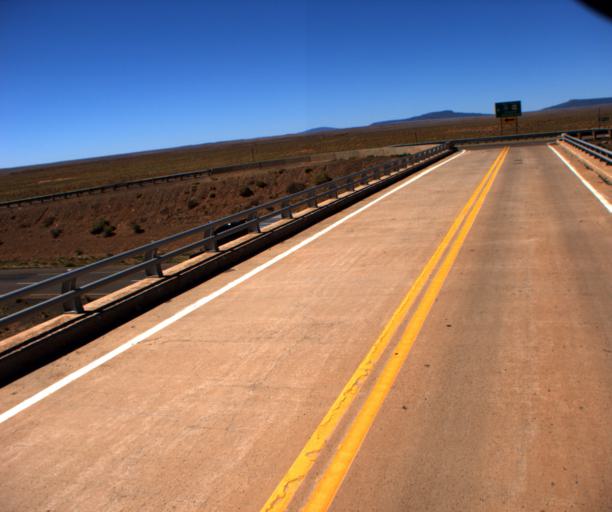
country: US
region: Arizona
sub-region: Coconino County
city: LeChee
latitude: 35.0676
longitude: -110.8353
